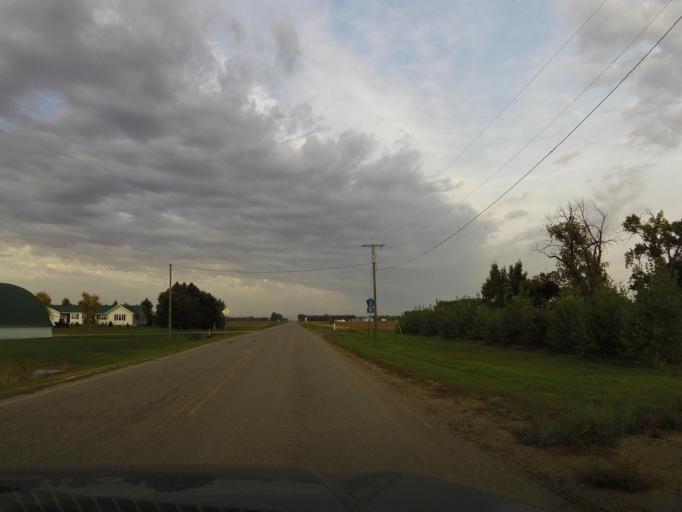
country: US
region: North Dakota
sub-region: Pembina County
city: Cavalier
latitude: 48.6882
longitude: -97.6690
